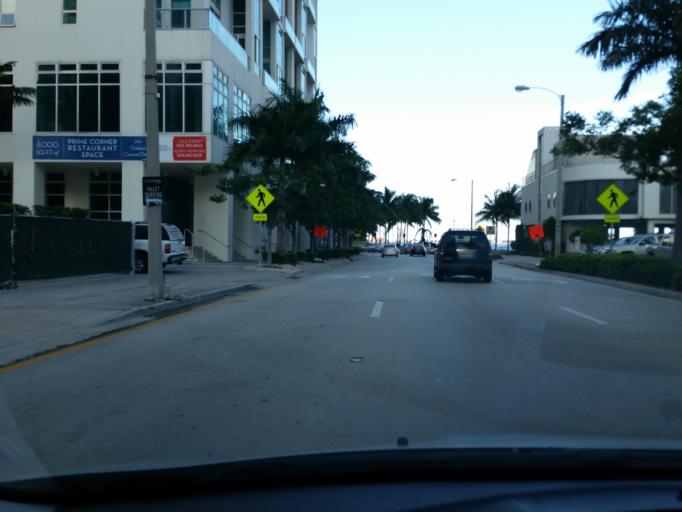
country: US
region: Florida
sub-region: Miami-Dade County
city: Miami
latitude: 25.7710
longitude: -80.1884
